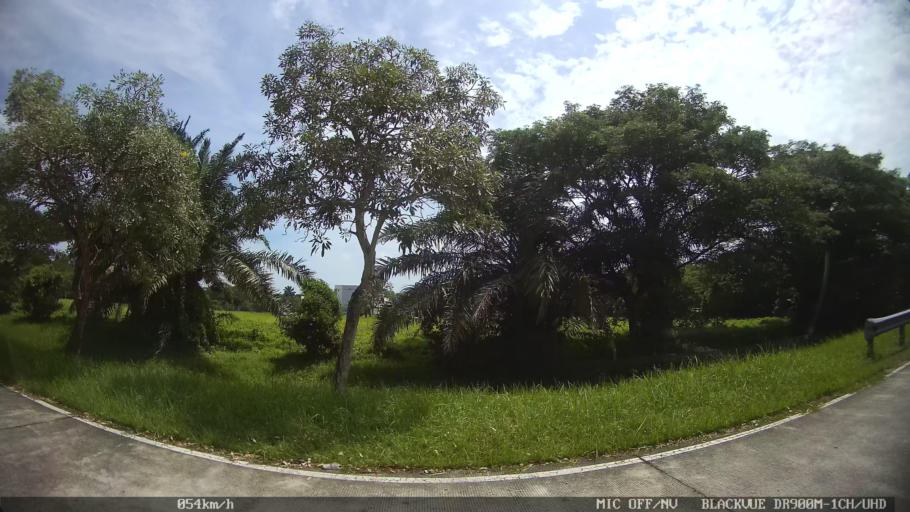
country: ID
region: North Sumatra
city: Percut
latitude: 3.6233
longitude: 98.8664
